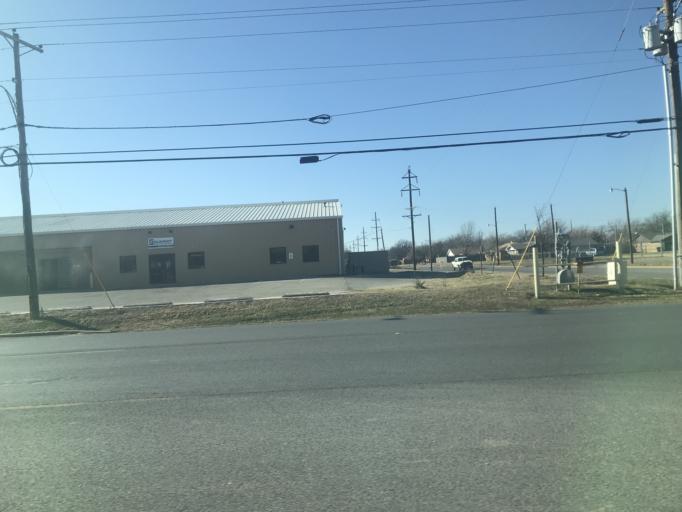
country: US
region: Texas
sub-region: Taylor County
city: Abilene
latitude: 32.4121
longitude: -99.7424
